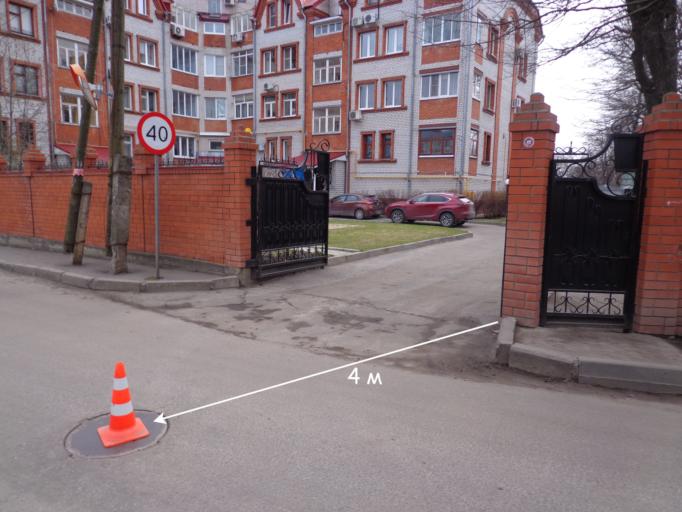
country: RU
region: Voronezj
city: Voronezh
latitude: 51.7050
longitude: 39.2304
